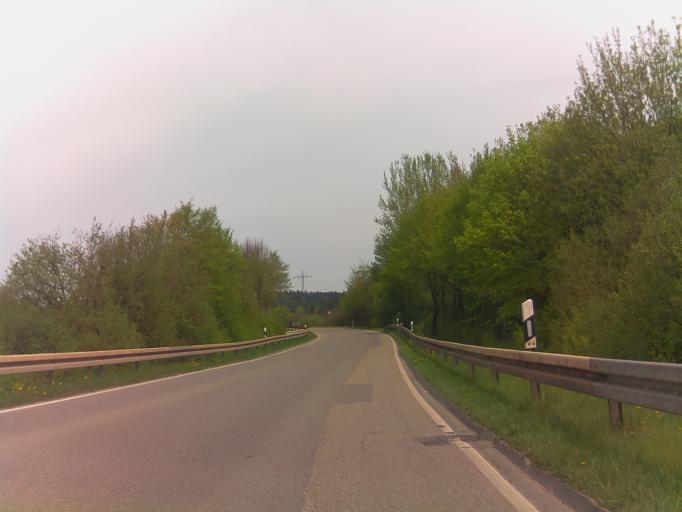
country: DE
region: Baden-Wuerttemberg
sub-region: Freiburg Region
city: Deisslingen
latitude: 48.0825
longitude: 8.5866
